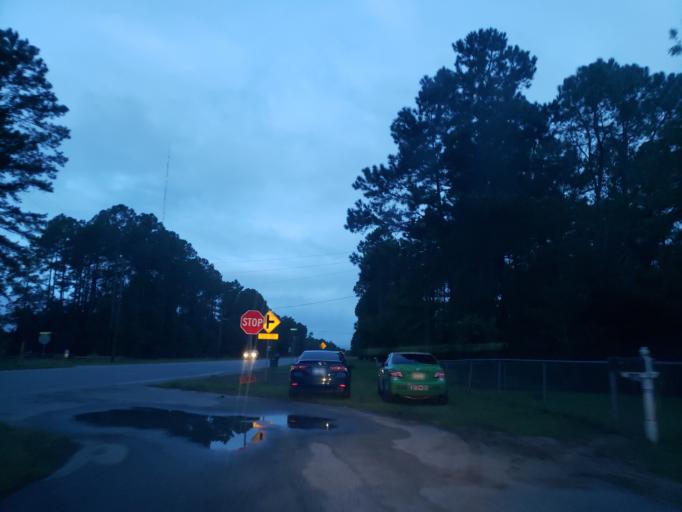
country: US
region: Georgia
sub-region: Chatham County
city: Bloomingdale
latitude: 32.0490
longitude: -81.3389
